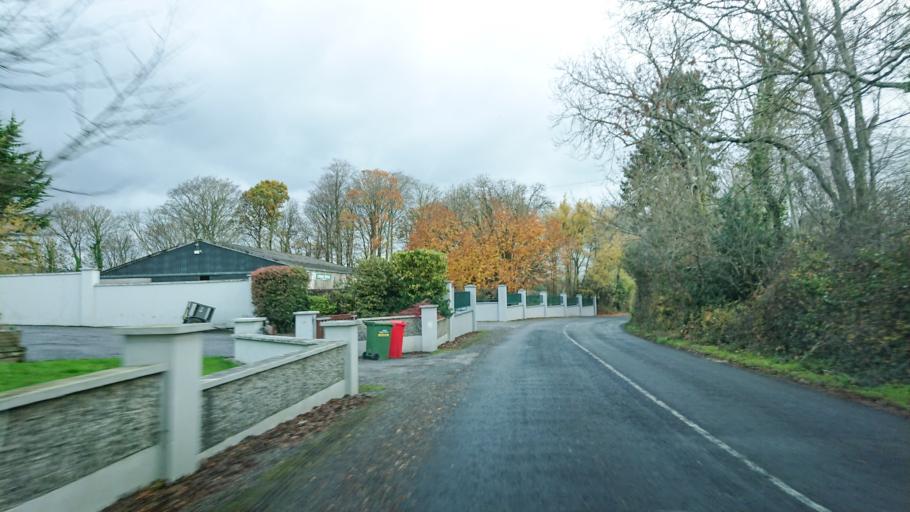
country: IE
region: Munster
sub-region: South Tipperary
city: Cluain Meala
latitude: 52.3537
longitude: -7.6482
